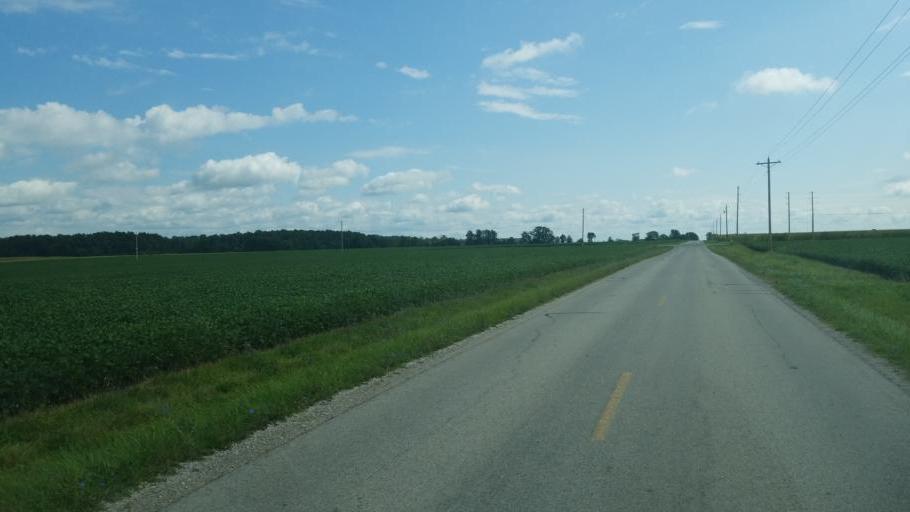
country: US
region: Ohio
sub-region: Seneca County
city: Tiffin
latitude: 41.0665
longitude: -83.0567
